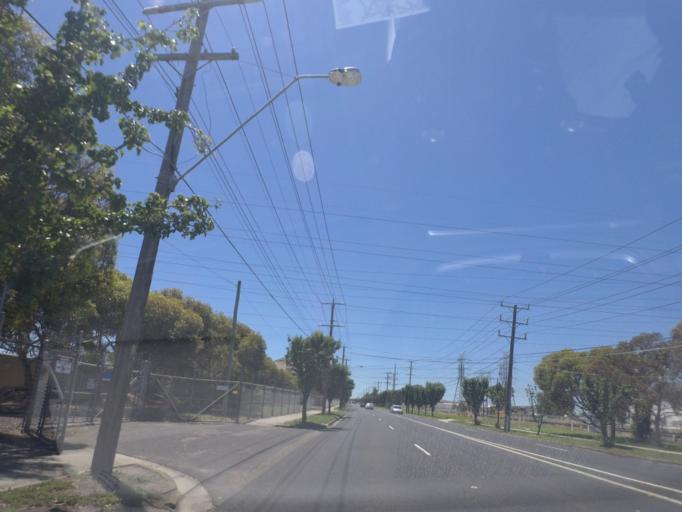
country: AU
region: Victoria
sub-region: Whittlesea
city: Thomastown
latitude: -37.6935
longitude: 145.0116
